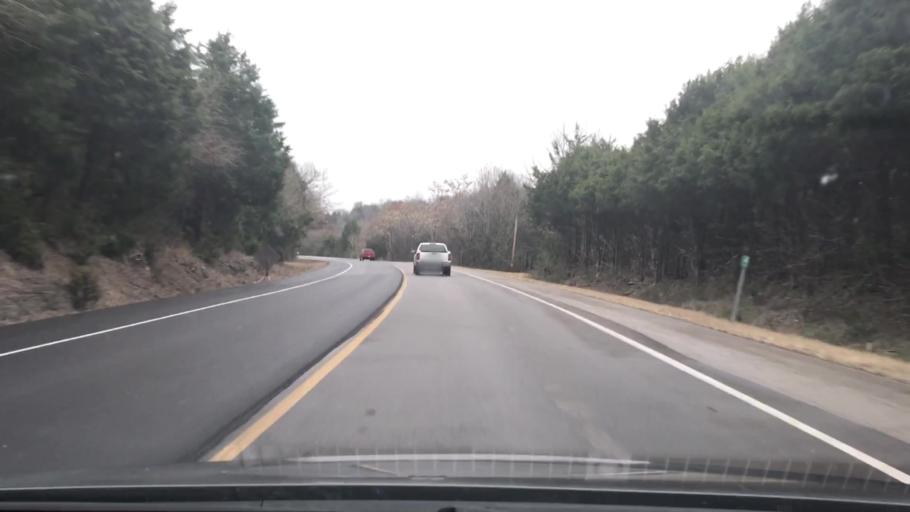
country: US
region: Tennessee
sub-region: Smith County
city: Carthage
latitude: 36.3260
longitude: -86.0217
